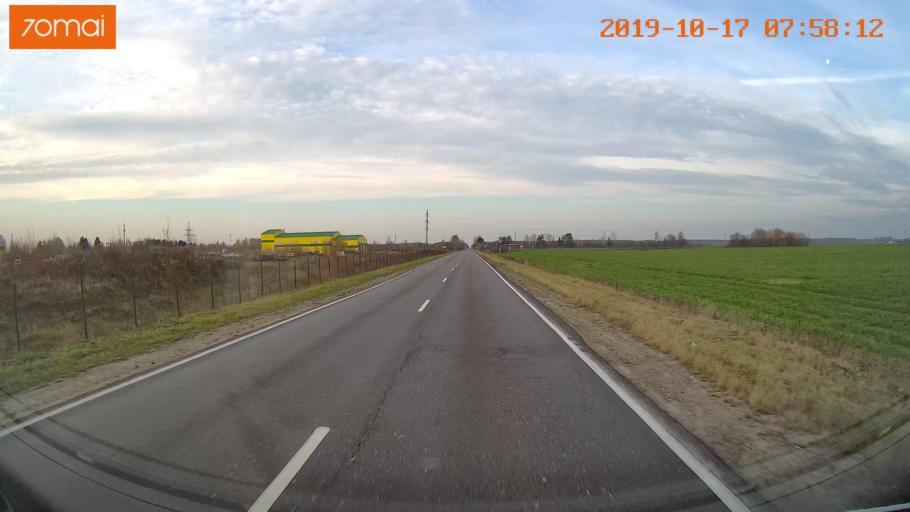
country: RU
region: Vladimir
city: Bavleny
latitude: 56.4049
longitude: 39.5623
